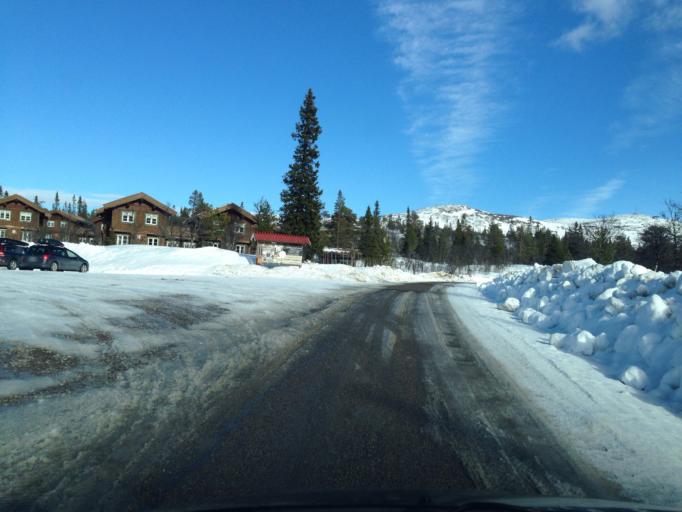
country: SE
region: Jaemtland
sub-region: Harjedalens Kommun
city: Sveg
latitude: 62.1328
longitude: 13.2797
